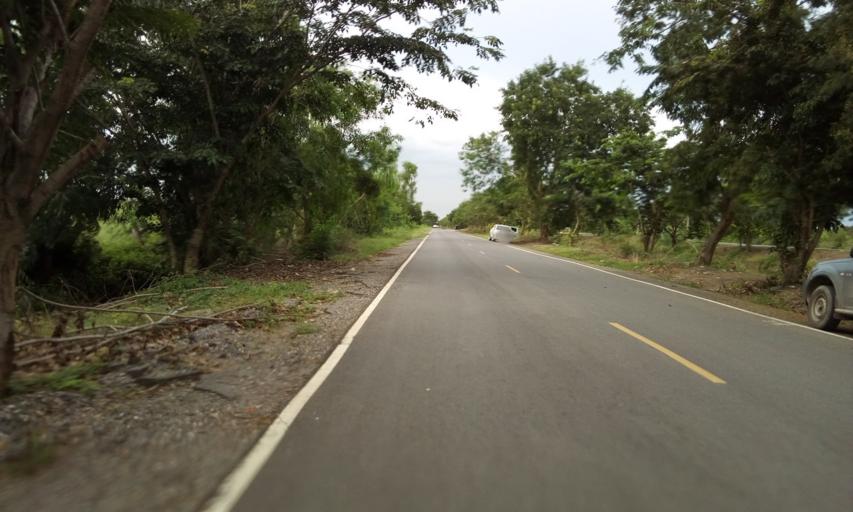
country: TH
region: Pathum Thani
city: Nong Suea
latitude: 14.2288
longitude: 100.8229
